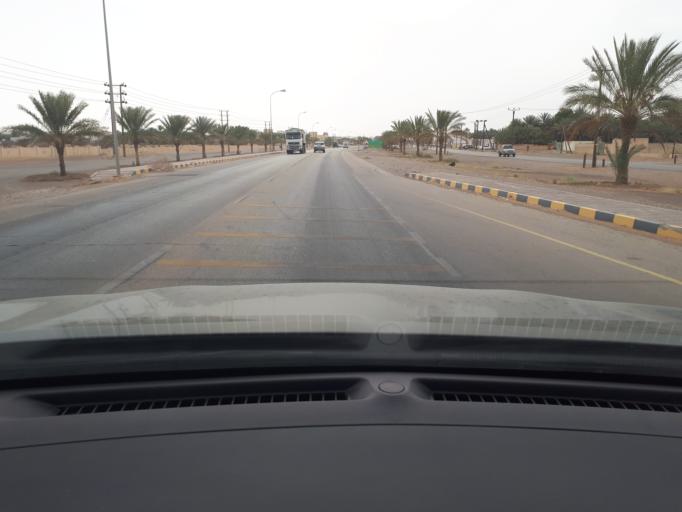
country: OM
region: Ash Sharqiyah
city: Badiyah
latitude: 22.4506
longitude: 58.8179
